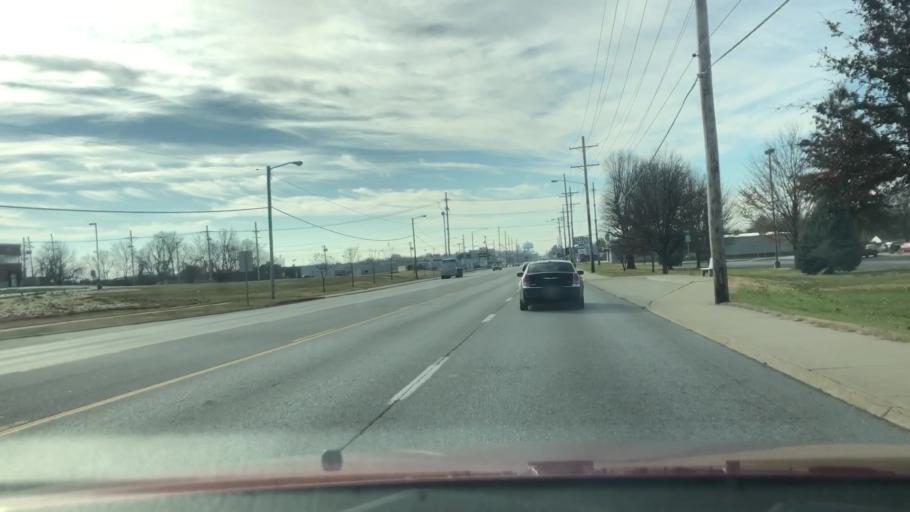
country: US
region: Missouri
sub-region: Greene County
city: Springfield
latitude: 37.2200
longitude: -93.2617
